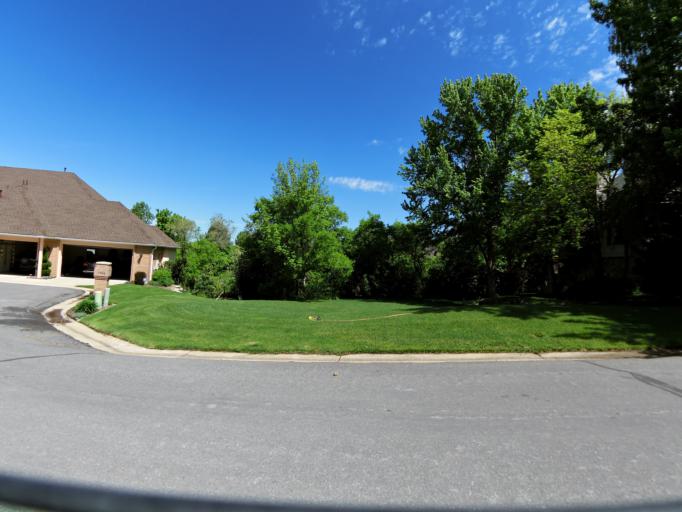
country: US
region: Utah
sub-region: Weber County
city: Uintah
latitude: 41.1772
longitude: -111.9365
